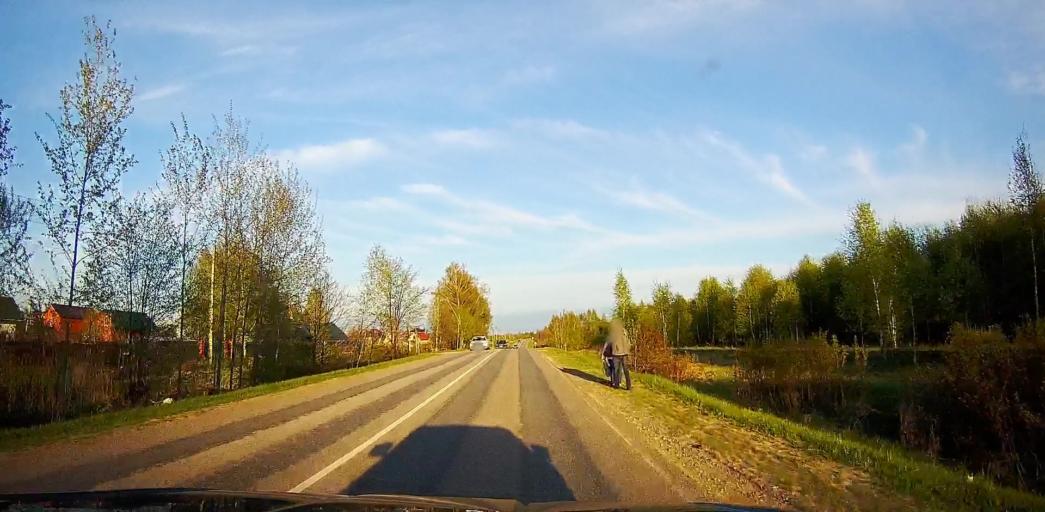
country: RU
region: Moskovskaya
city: Meshcherino
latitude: 55.2503
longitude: 38.2869
